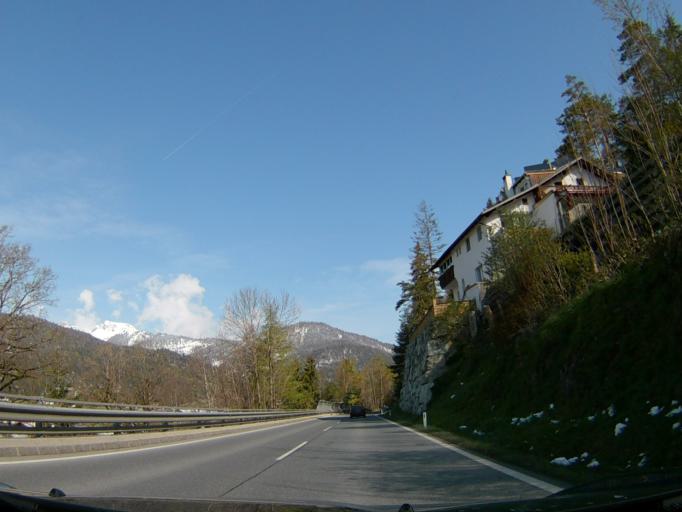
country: AT
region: Tyrol
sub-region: Politischer Bezirk Schwaz
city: Achenkirch
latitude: 47.5012
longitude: 11.7092
